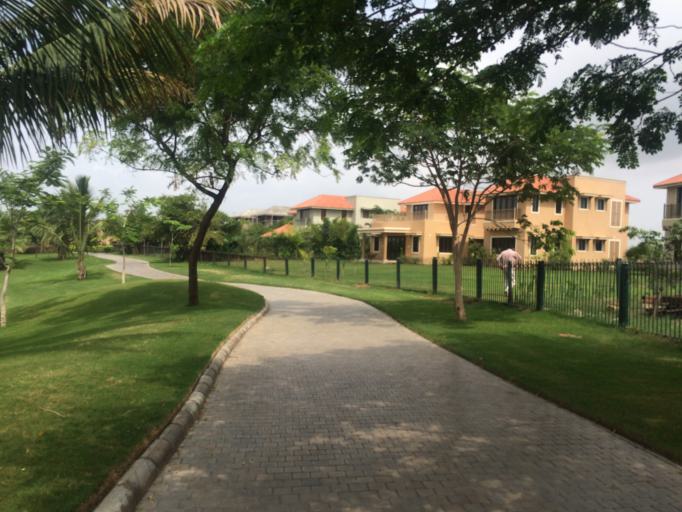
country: IN
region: Gujarat
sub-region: Ahmadabad
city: Sanand
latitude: 23.0227
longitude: 72.3599
